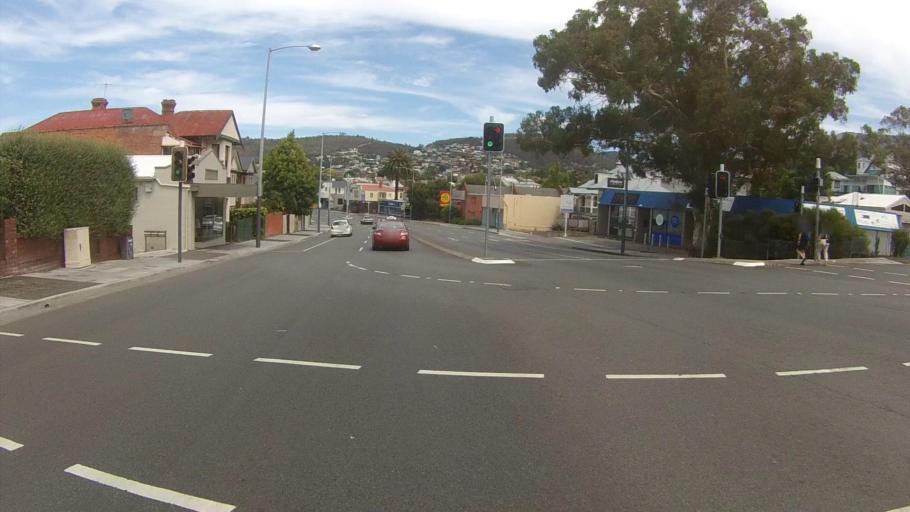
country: AU
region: Tasmania
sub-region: Hobart
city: Sandy Bay
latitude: -42.8920
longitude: 147.3265
